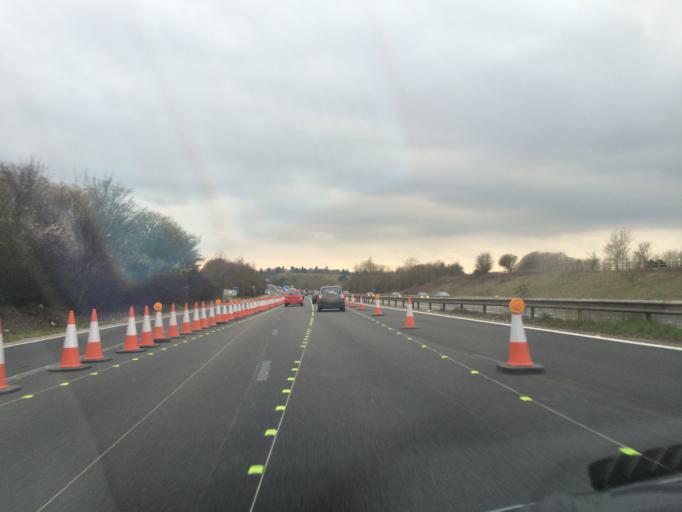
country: GB
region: England
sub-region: West Berkshire
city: Welford
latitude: 51.4508
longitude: -1.3965
